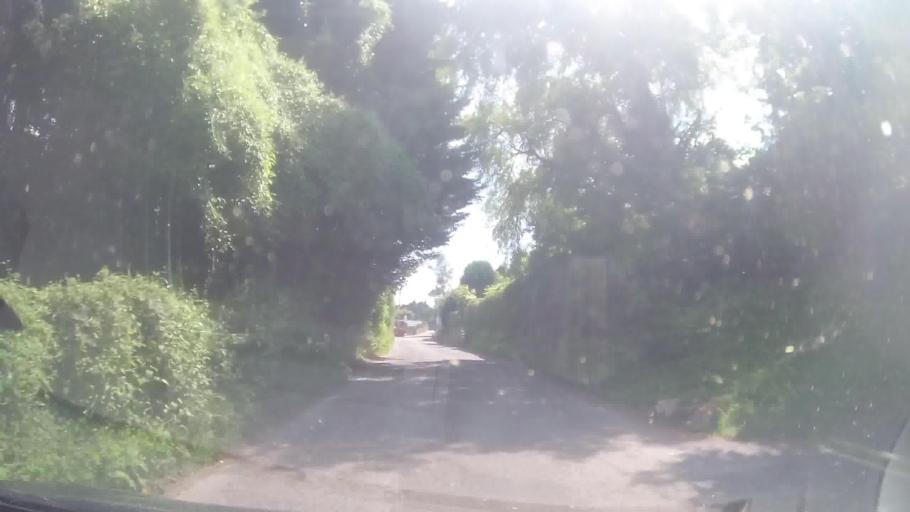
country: GB
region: England
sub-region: Herefordshire
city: Whitchurch
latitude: 51.8502
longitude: -2.6489
